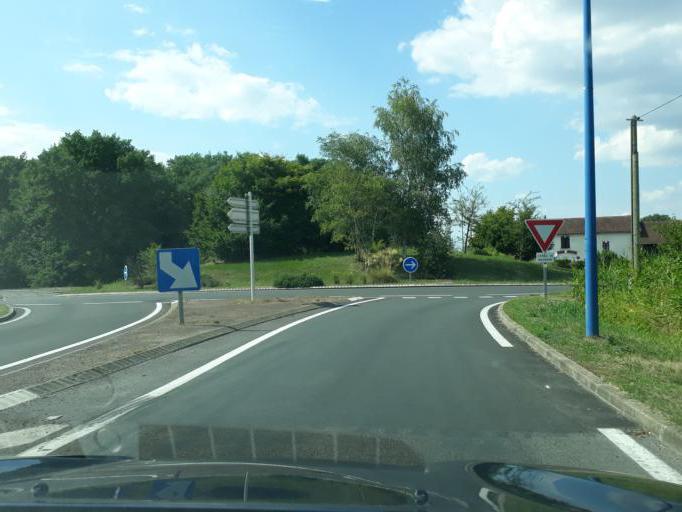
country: FR
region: Bourgogne
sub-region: Departement de la Nievre
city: Fourchambault
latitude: 47.0050
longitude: 3.0958
